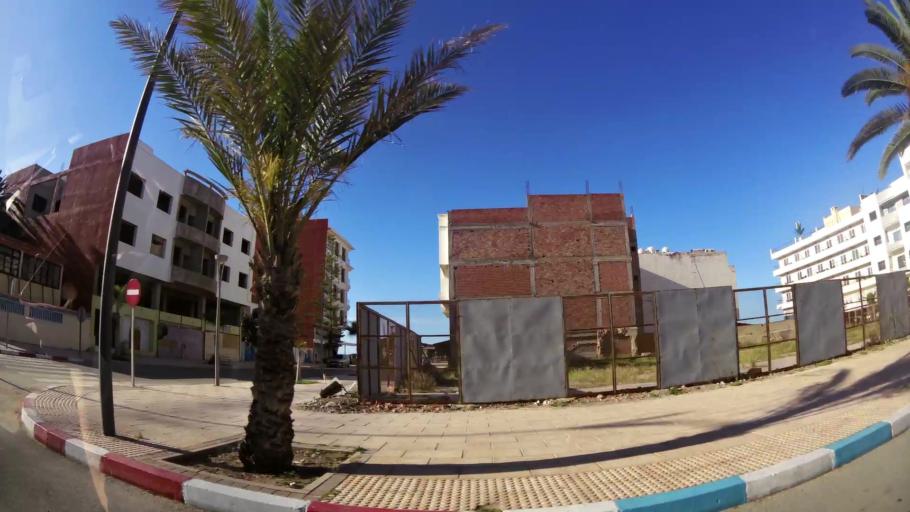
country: MA
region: Oriental
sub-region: Berkane-Taourirt
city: Madagh
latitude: 35.0856
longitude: -2.2240
